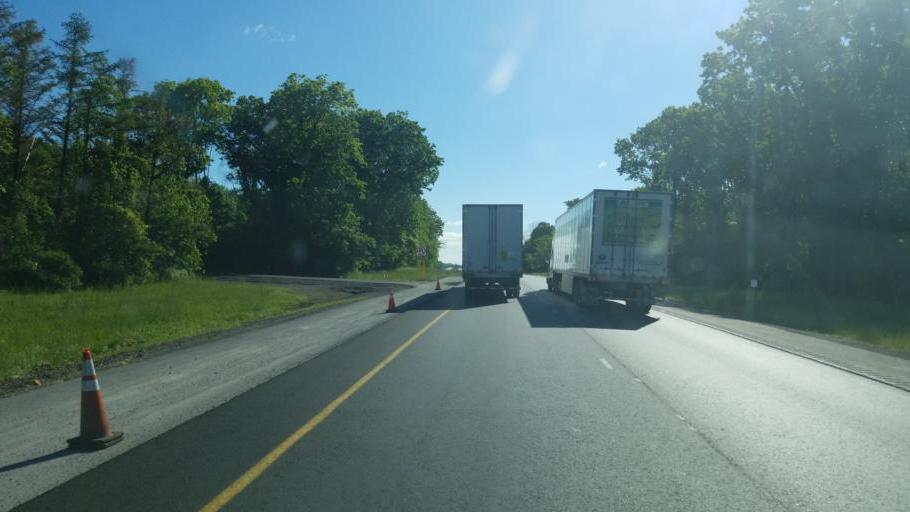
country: US
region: New York
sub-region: Livingston County
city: Caledonia
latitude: 43.0309
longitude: -77.8279
